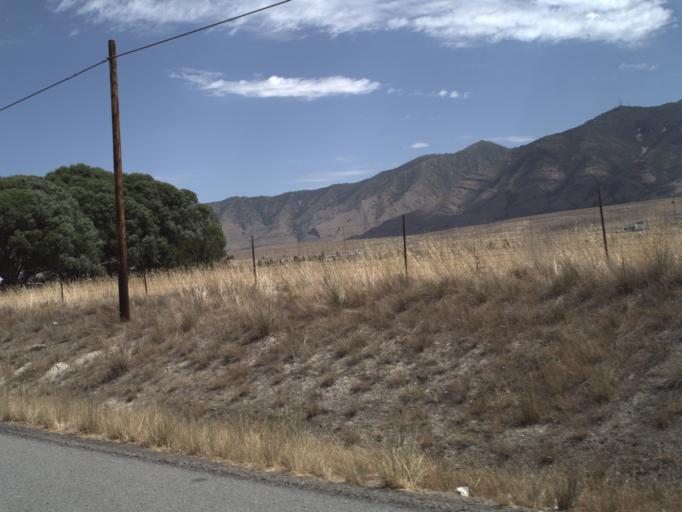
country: US
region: Utah
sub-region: Tooele County
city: Erda
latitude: 40.6109
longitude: -112.2943
